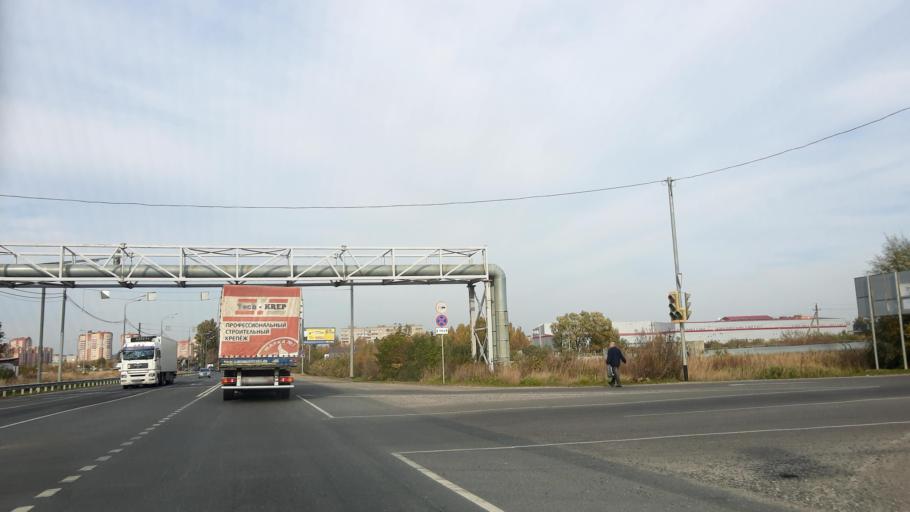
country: RU
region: Moskovskaya
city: Elektrostal'
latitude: 55.7573
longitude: 38.4402
